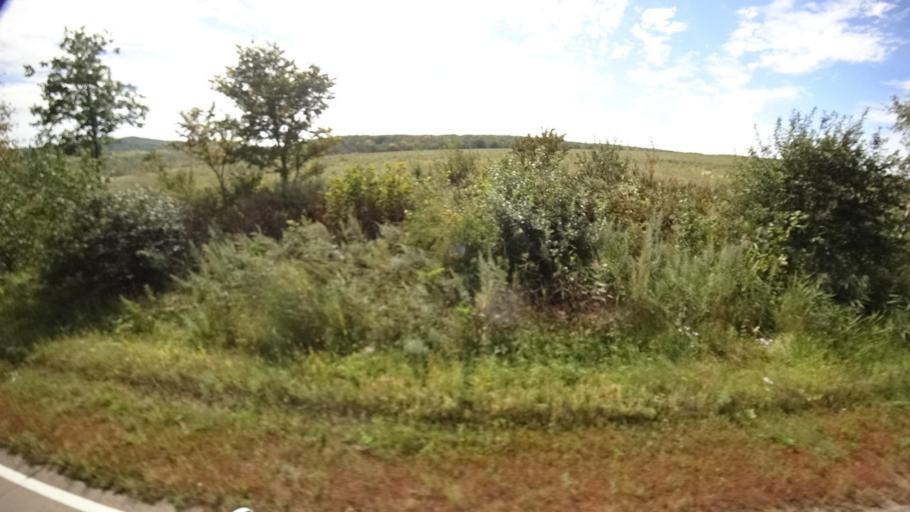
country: RU
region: Primorskiy
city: Yakovlevka
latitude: 44.4122
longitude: 133.5870
